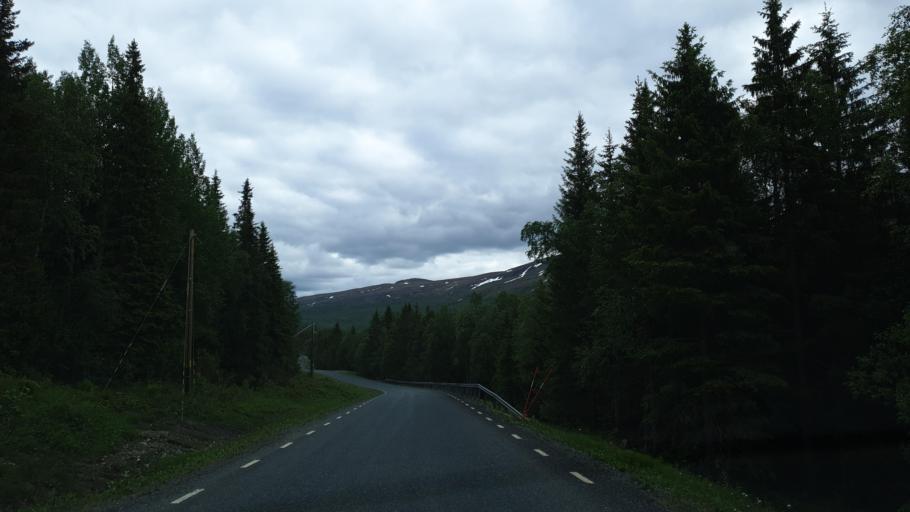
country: NO
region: Nordland
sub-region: Hattfjelldal
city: Hattfjelldal
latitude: 65.4376
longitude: 14.5696
